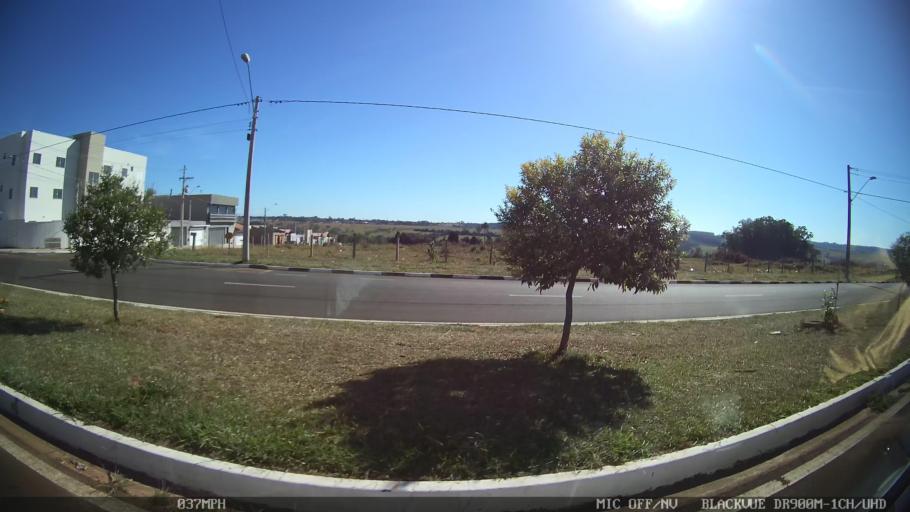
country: BR
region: Sao Paulo
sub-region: Franca
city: Franca
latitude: -20.5644
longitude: -47.3463
